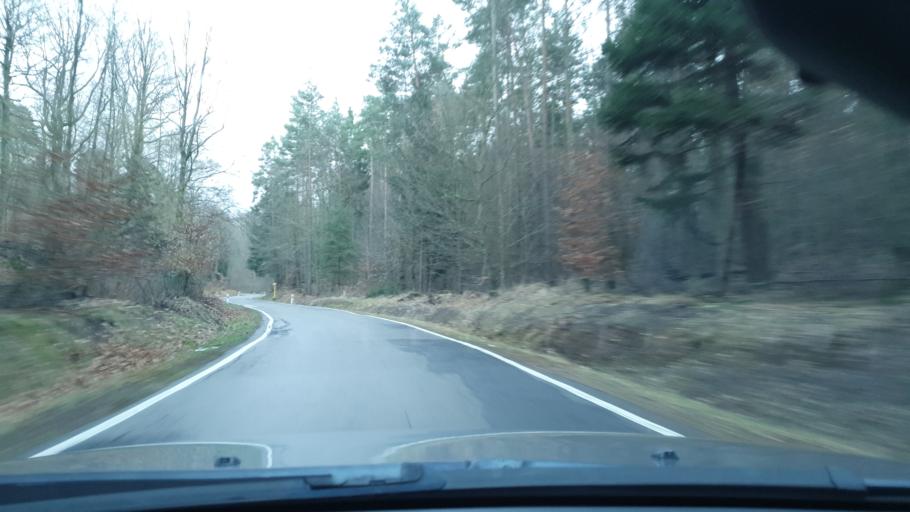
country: DE
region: Rheinland-Pfalz
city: Kaiserslautern
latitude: 49.4246
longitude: 7.7689
